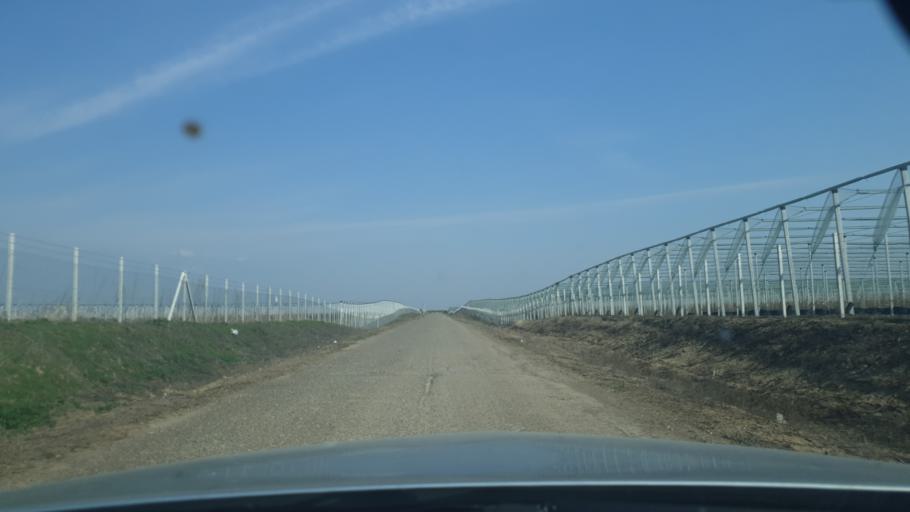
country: RS
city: Putinci
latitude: 45.0441
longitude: 19.9496
